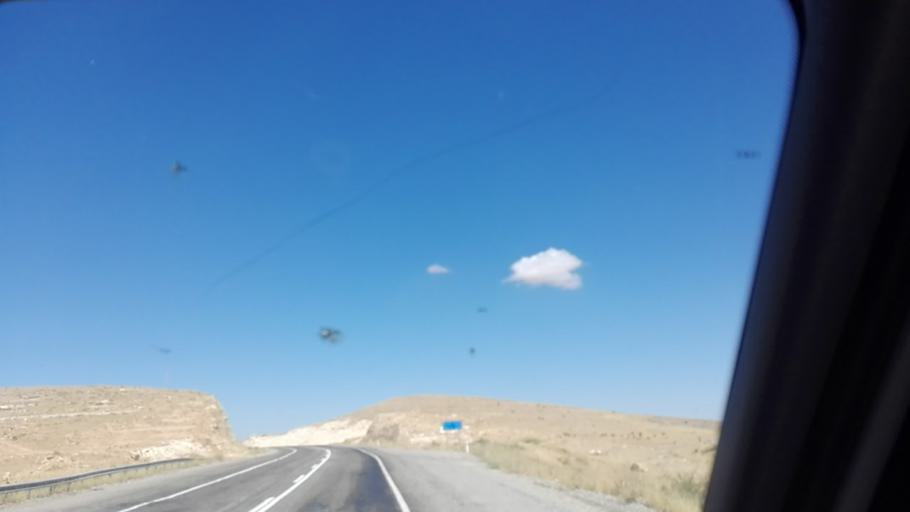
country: TR
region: Batman
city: Gerdzhyush
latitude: 37.5554
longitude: 41.3632
